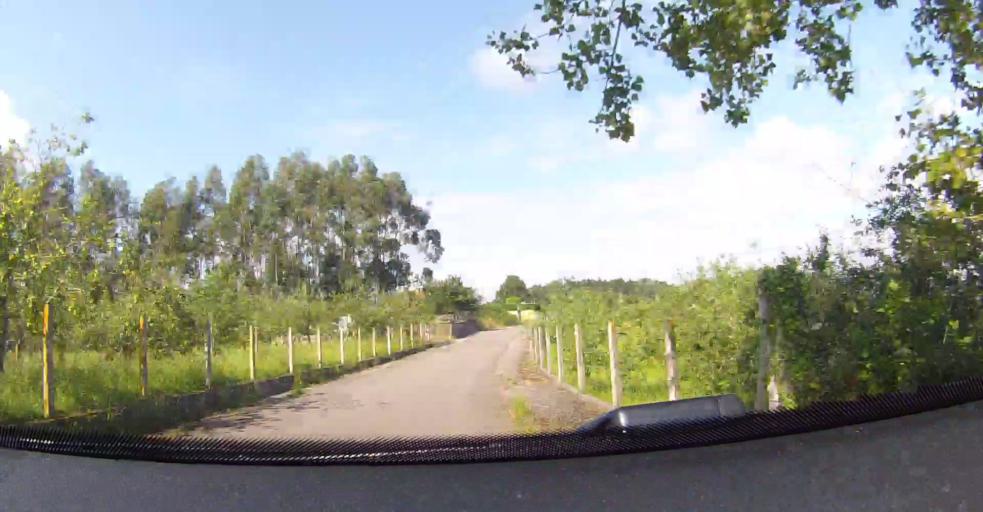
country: ES
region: Asturias
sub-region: Province of Asturias
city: Villaviciosa
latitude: 43.4864
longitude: -5.3928
